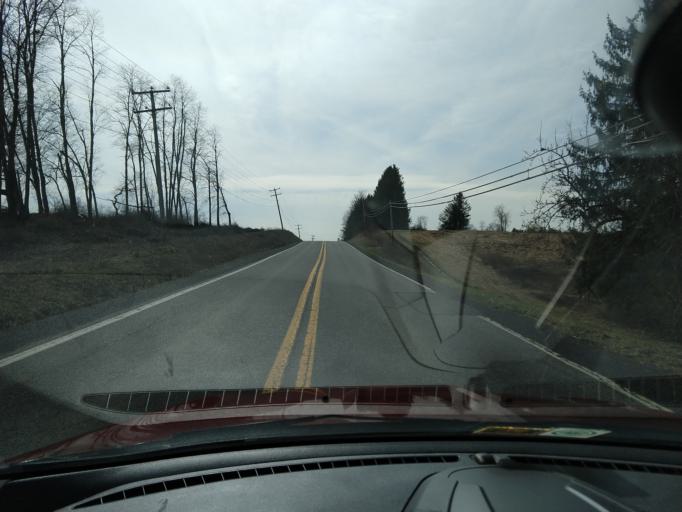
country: US
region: West Virginia
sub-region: Greenbrier County
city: Lewisburg
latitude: 37.8832
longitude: -80.4136
